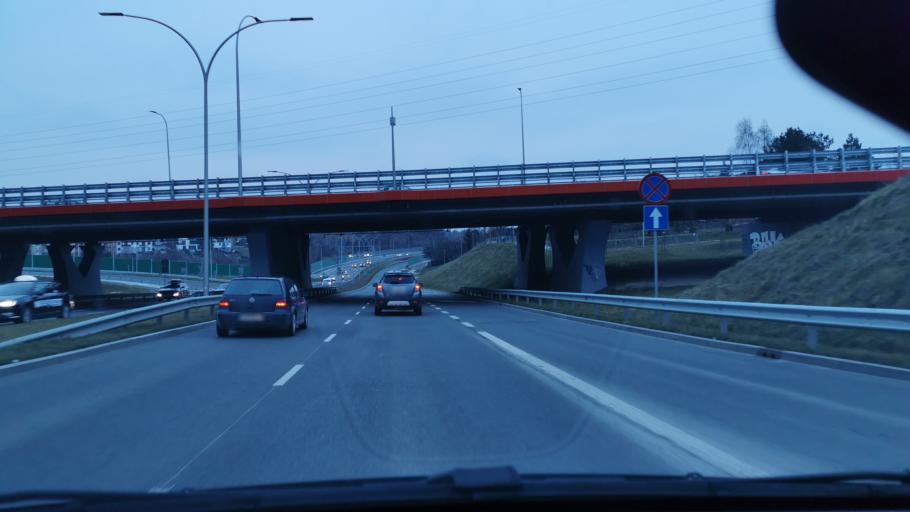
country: PL
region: Lublin Voivodeship
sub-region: Powiat lubelski
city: Lublin
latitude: 51.2516
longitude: 22.5046
